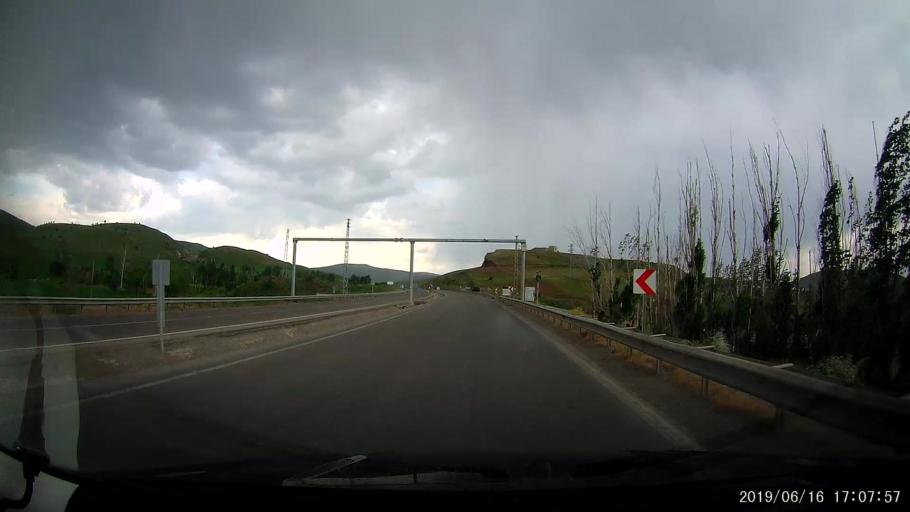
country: TR
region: Erzurum
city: Askale
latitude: 39.9150
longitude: 40.6668
